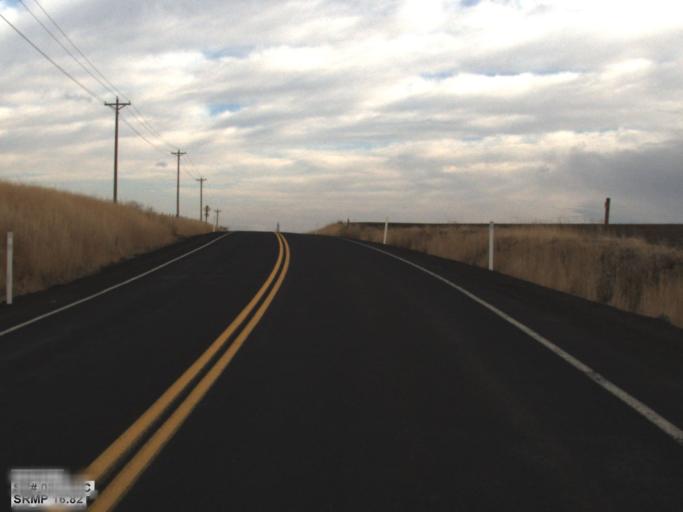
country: US
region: Washington
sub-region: Lincoln County
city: Davenport
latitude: 47.8609
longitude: -118.2415
